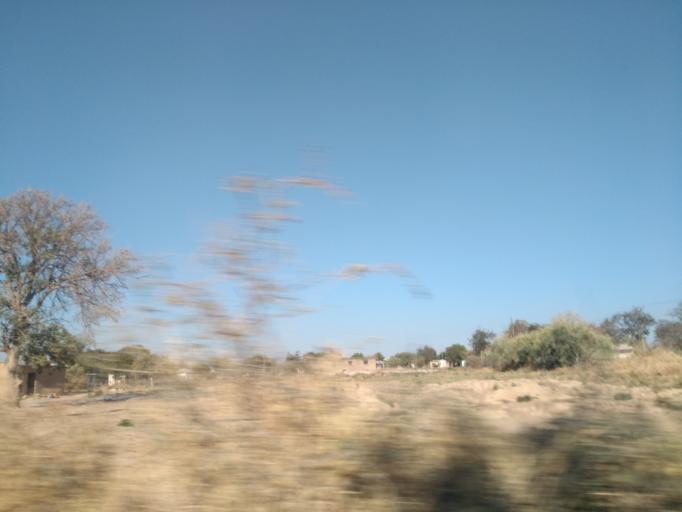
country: TZ
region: Dodoma
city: Dodoma
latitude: -6.1305
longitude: 35.7397
